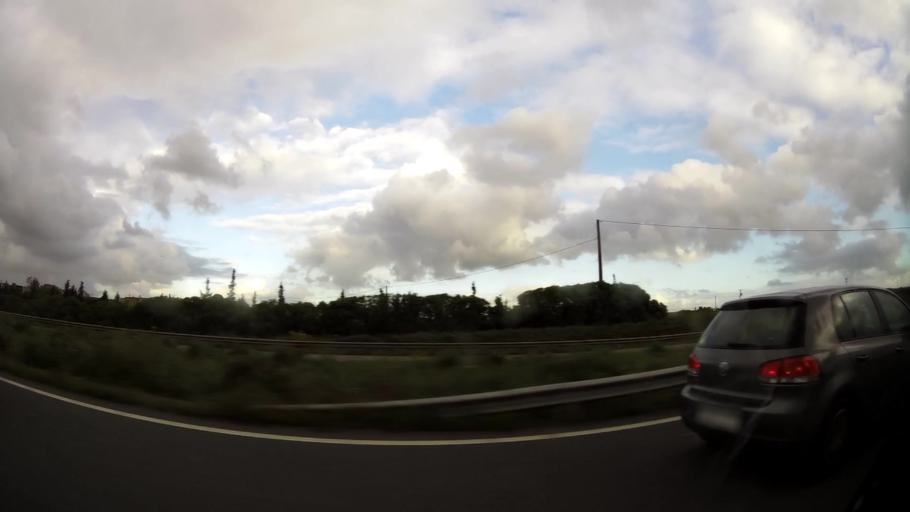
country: MA
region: Grand Casablanca
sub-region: Mohammedia
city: Mohammedia
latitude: 33.6225
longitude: -7.4306
